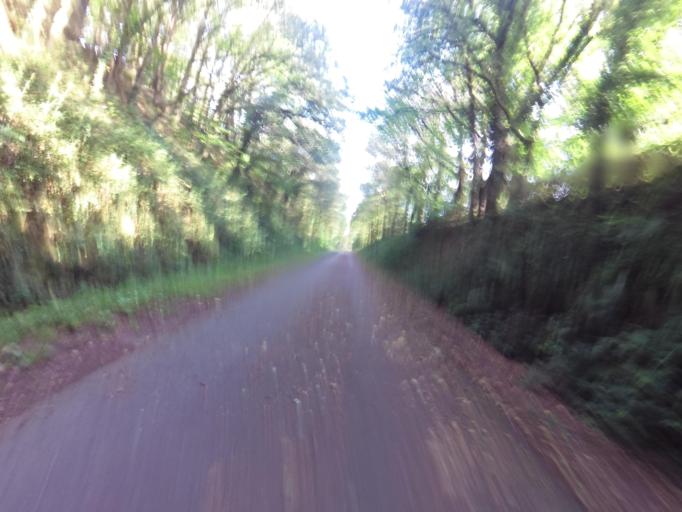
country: FR
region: Brittany
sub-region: Departement du Morbihan
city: Ploermel
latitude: 47.9147
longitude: -2.4293
